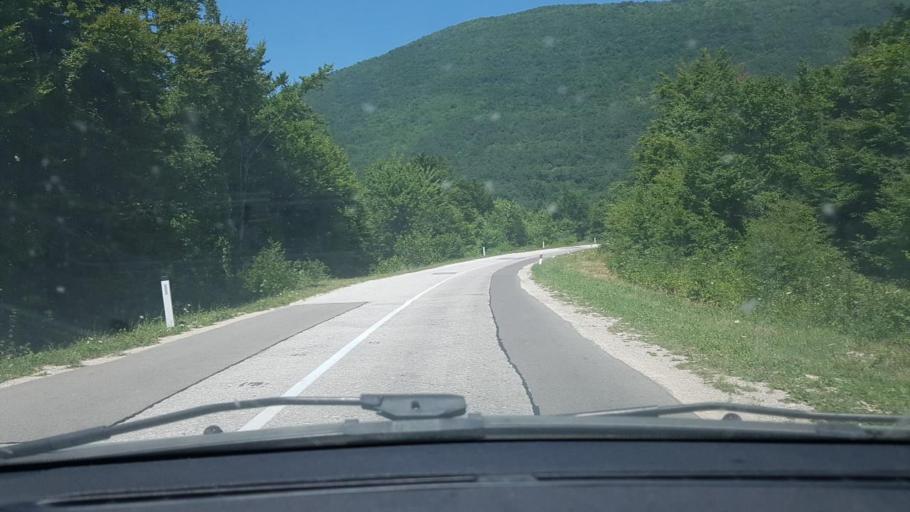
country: BA
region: Federation of Bosnia and Herzegovina
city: Orasac
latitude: 44.7119
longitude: 16.0375
